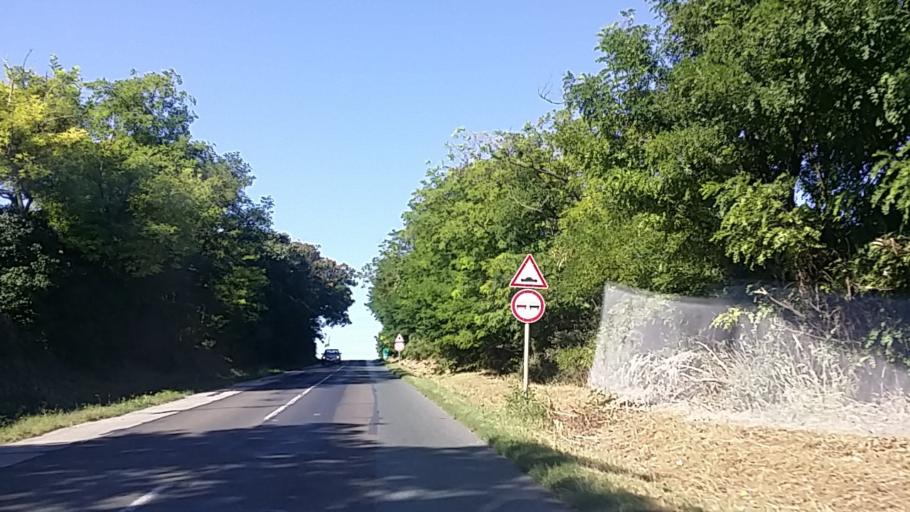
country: HU
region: Fejer
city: dunaujvaros
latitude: 46.9702
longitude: 18.8991
